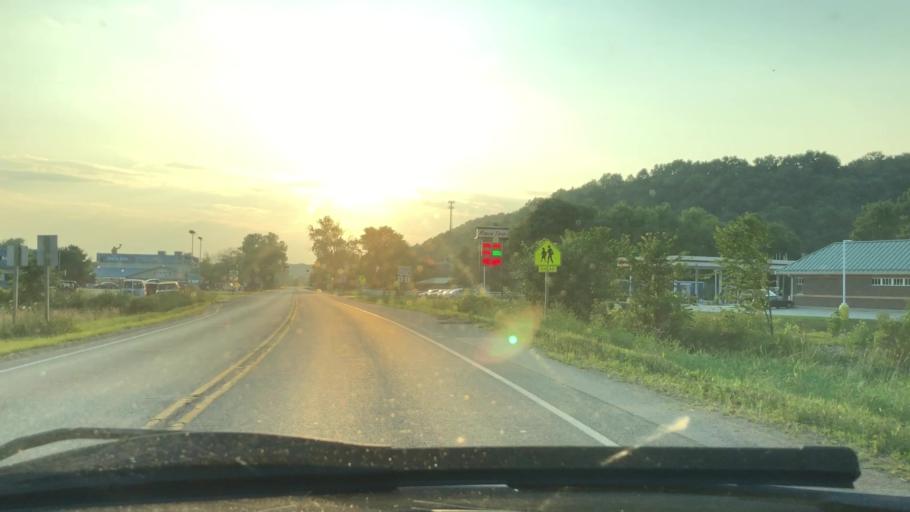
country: US
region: Wisconsin
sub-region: Dane County
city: Black Earth
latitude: 43.1424
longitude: -89.7453
